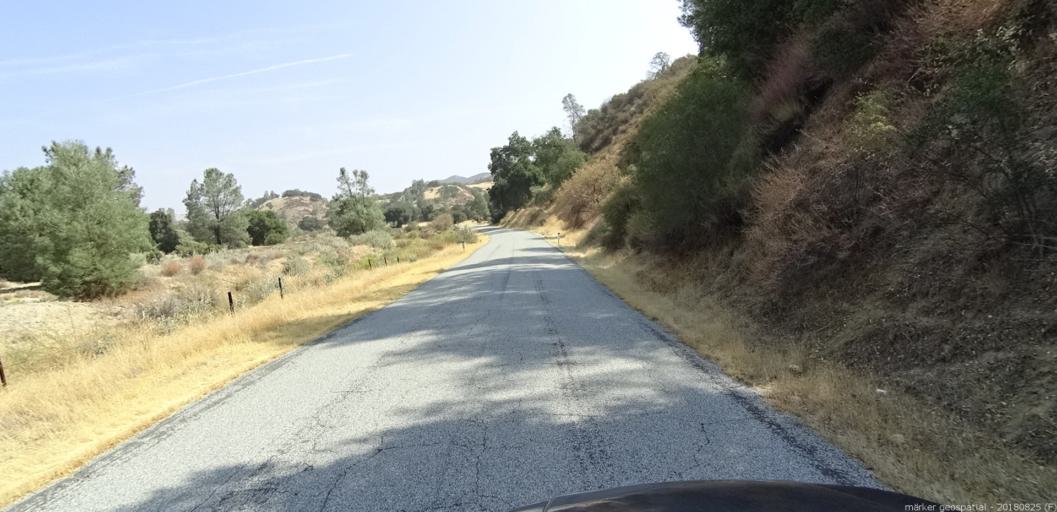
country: US
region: California
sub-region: San Luis Obispo County
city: San Miguel
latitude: 35.8843
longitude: -120.5613
